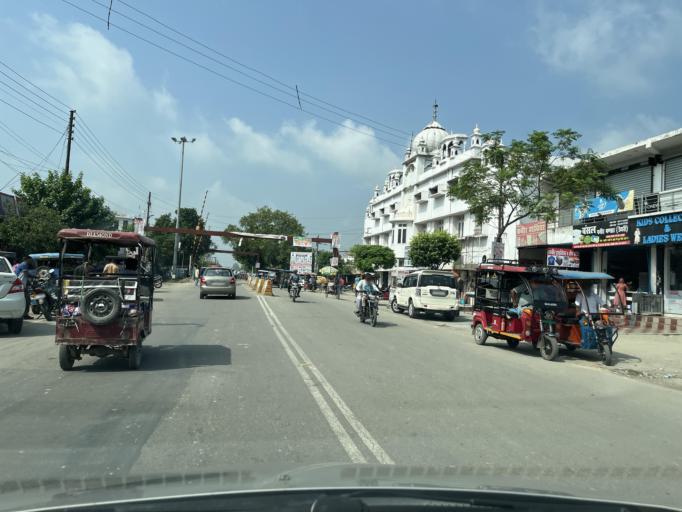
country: IN
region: Uttarakhand
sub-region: Udham Singh Nagar
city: Bazpur
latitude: 29.1581
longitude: 79.1501
